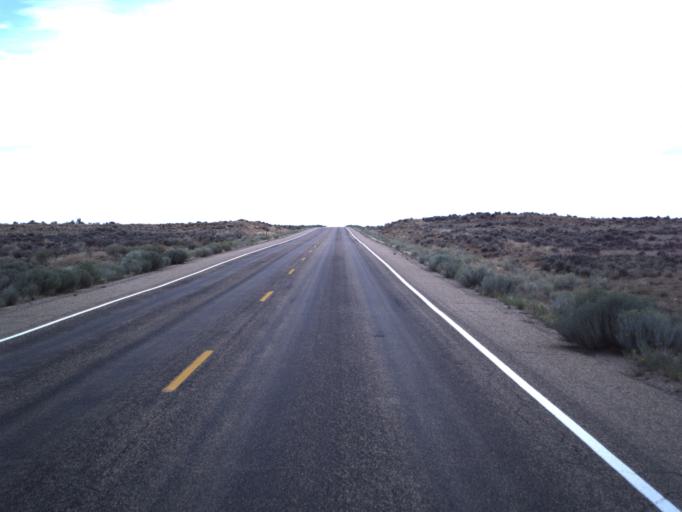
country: US
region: Utah
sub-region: Uintah County
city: Naples
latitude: 40.1592
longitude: -109.3086
